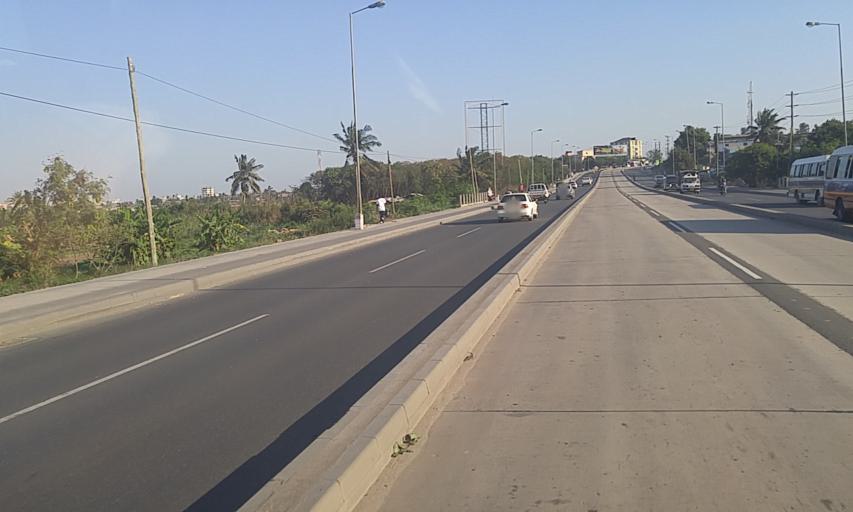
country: TZ
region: Dar es Salaam
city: Magomeni
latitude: -6.8004
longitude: 39.2625
